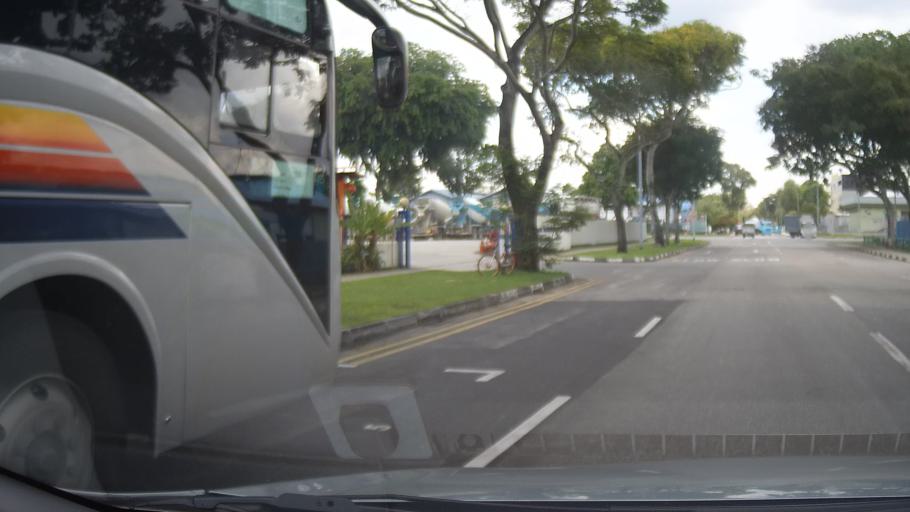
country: MY
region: Johor
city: Johor Bahru
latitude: 1.3267
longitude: 103.6935
